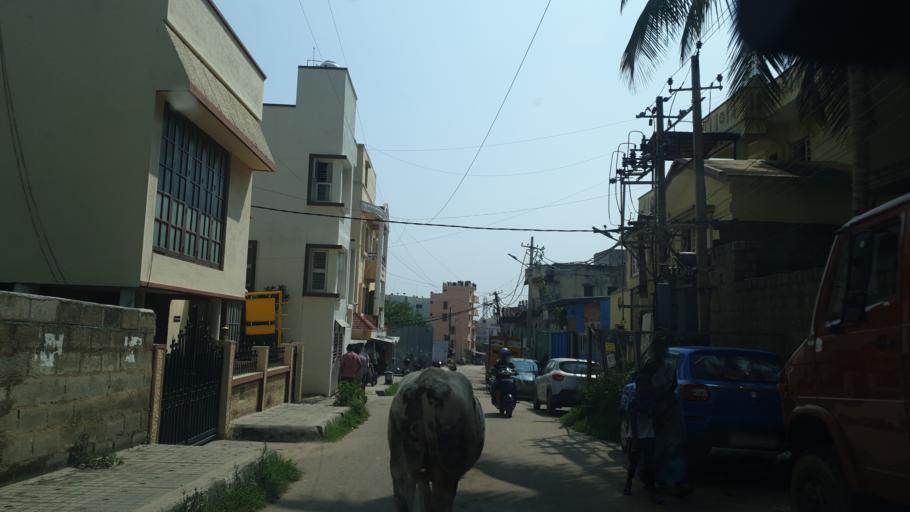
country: IN
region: Karnataka
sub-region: Bangalore Urban
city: Bangalore
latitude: 12.9688
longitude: 77.6668
